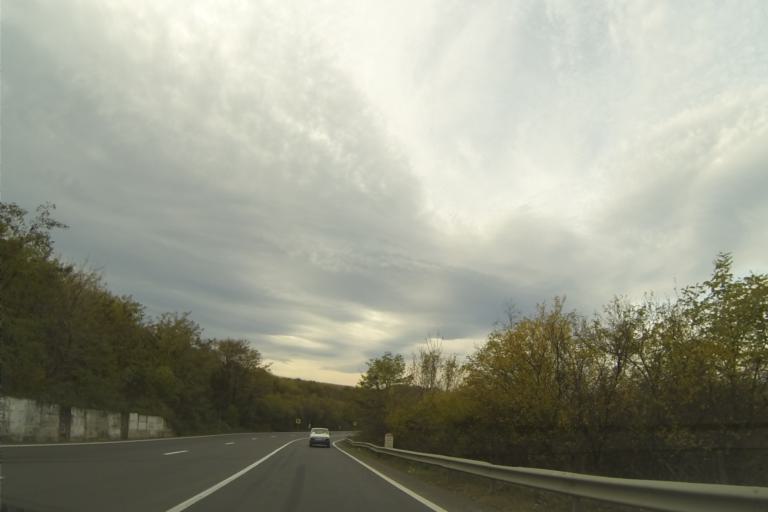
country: RO
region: Olt
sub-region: Comuna Scornicesti
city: Margineni Slobozia
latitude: 44.5375
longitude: 24.5392
